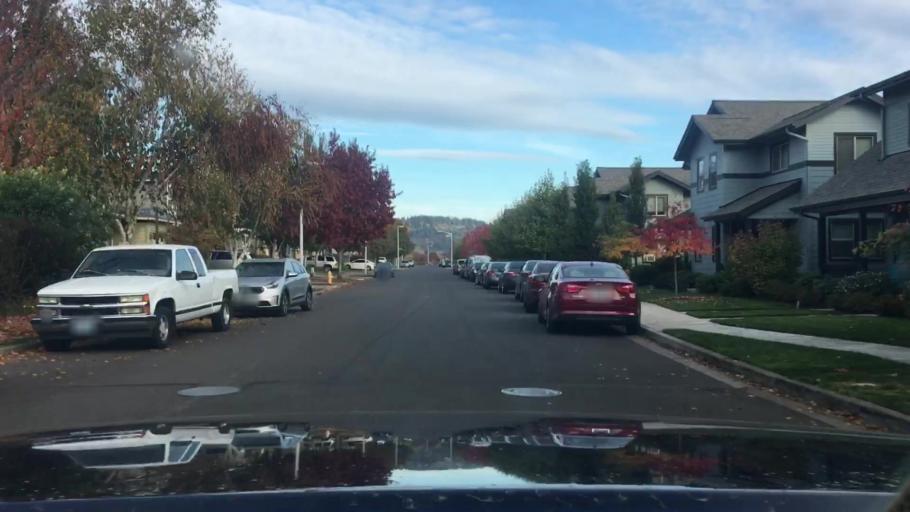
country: US
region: Oregon
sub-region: Lane County
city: Coburg
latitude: 44.0975
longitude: -123.0710
